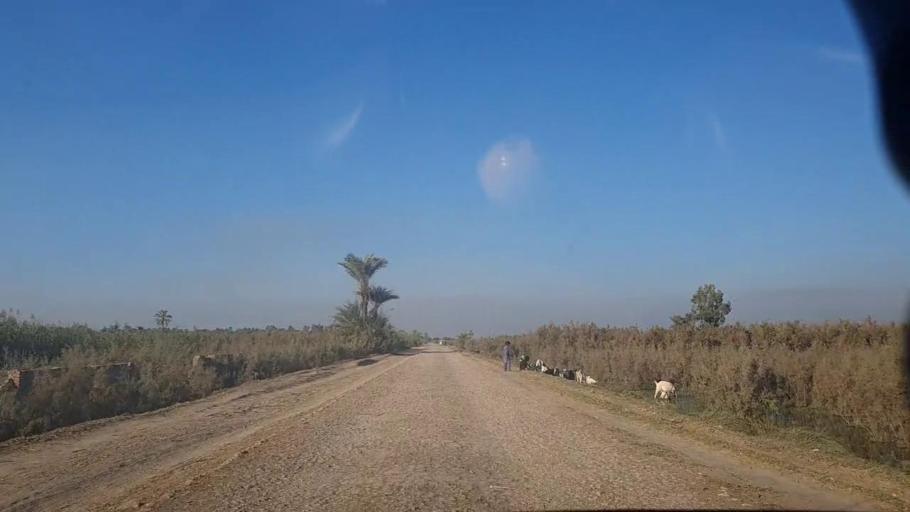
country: PK
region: Sindh
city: Sobhadero
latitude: 27.4033
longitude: 68.4217
